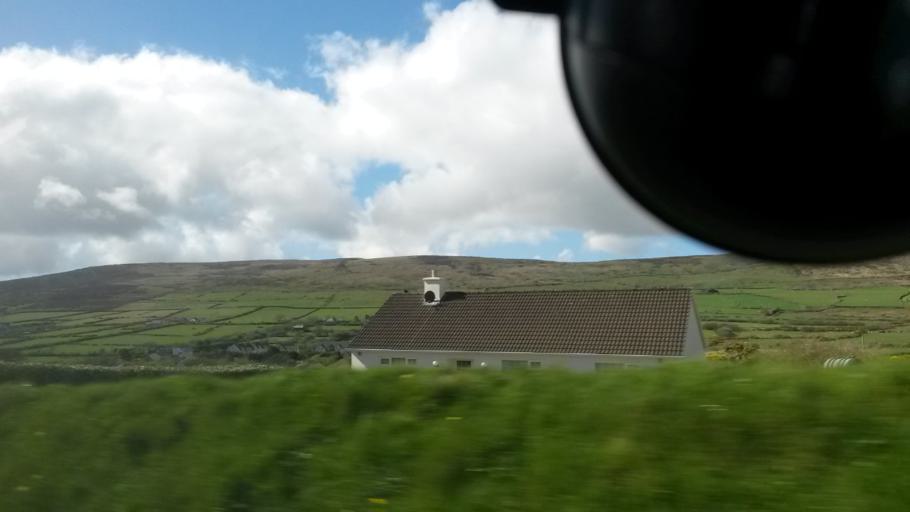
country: IE
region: Munster
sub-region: Ciarrai
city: Dingle
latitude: 52.1462
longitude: -10.2520
